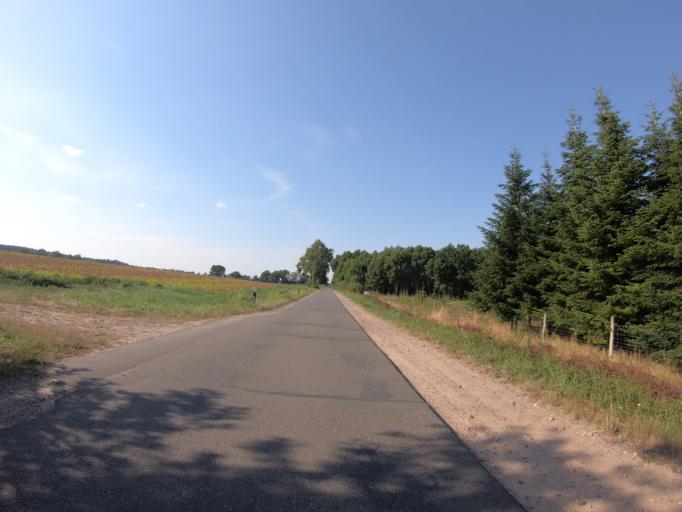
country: DE
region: Lower Saxony
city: Wieren
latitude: 52.8723
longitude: 10.6591
